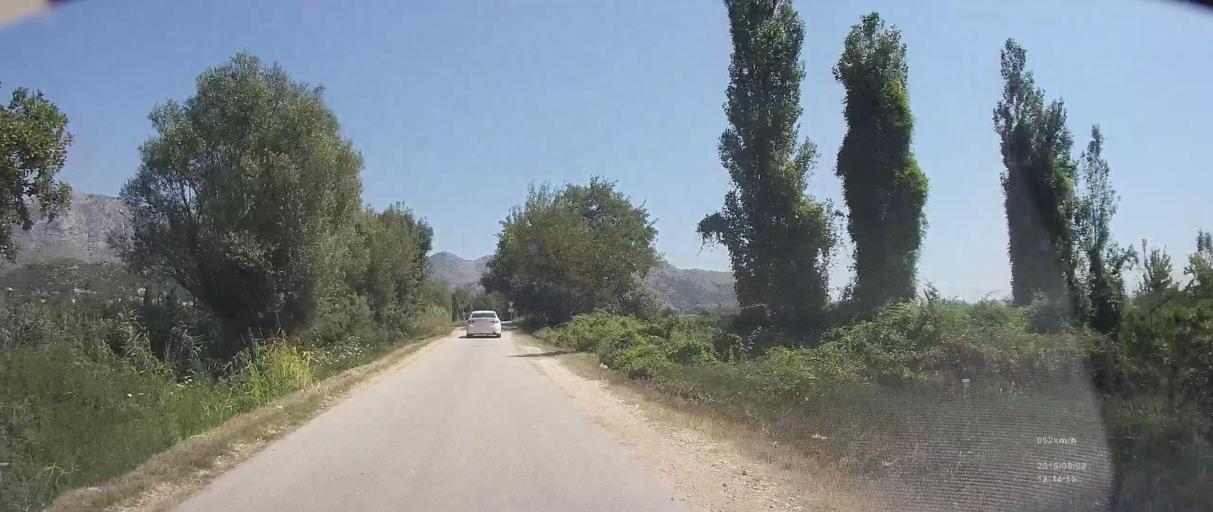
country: HR
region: Dubrovacko-Neretvanska
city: Komin
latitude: 43.0404
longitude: 17.4946
